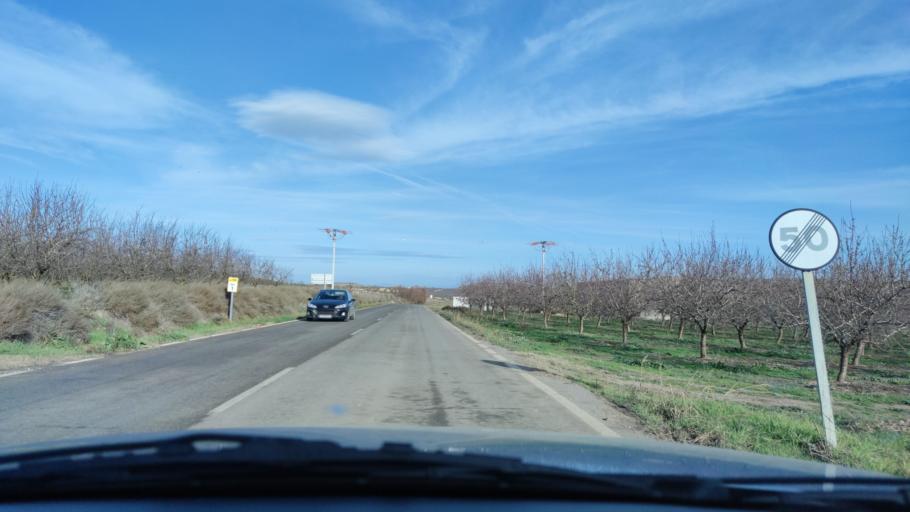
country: ES
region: Catalonia
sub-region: Provincia de Lleida
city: Alcano
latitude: 41.4838
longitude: 0.6163
